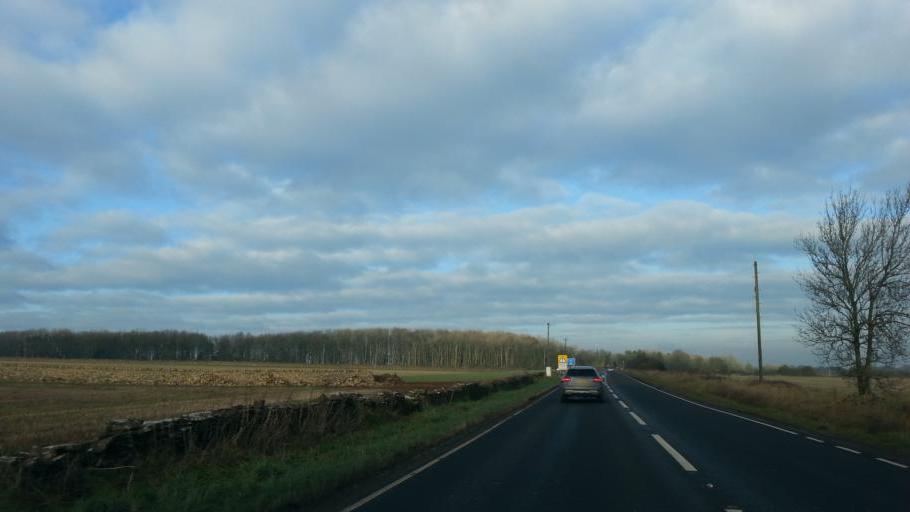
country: GB
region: England
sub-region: South Gloucestershire
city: Hinton
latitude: 51.4935
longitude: -2.3556
